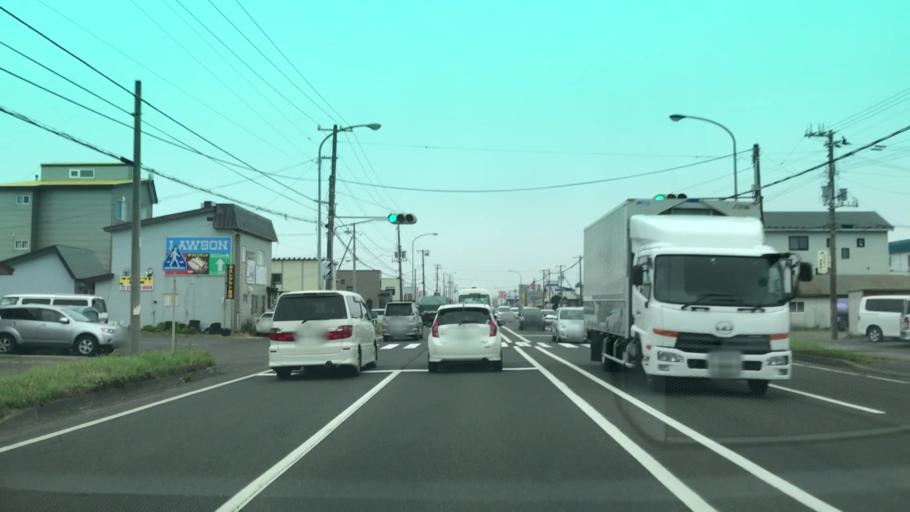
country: JP
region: Hokkaido
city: Muroran
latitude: 42.3774
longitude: 141.0701
